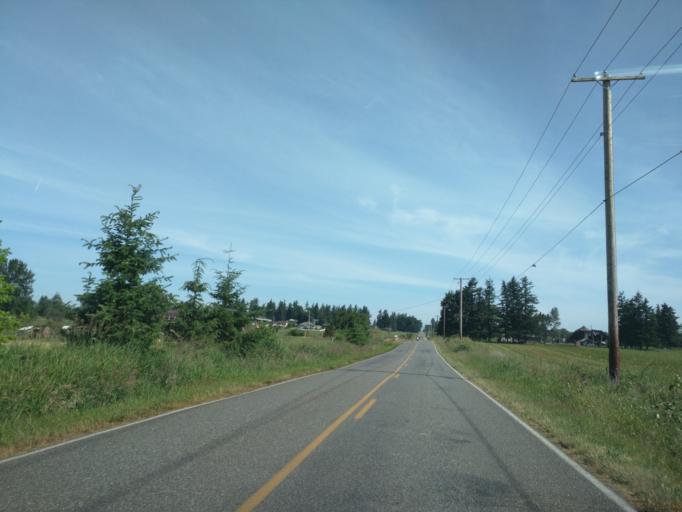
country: US
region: Washington
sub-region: Whatcom County
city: Lynden
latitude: 48.9502
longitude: -122.4078
